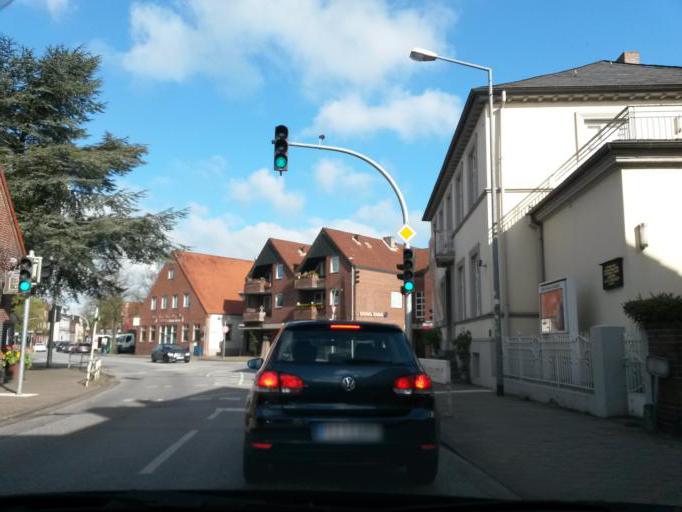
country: DE
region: Schleswig-Holstein
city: Wedel
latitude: 53.5835
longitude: 9.6991
